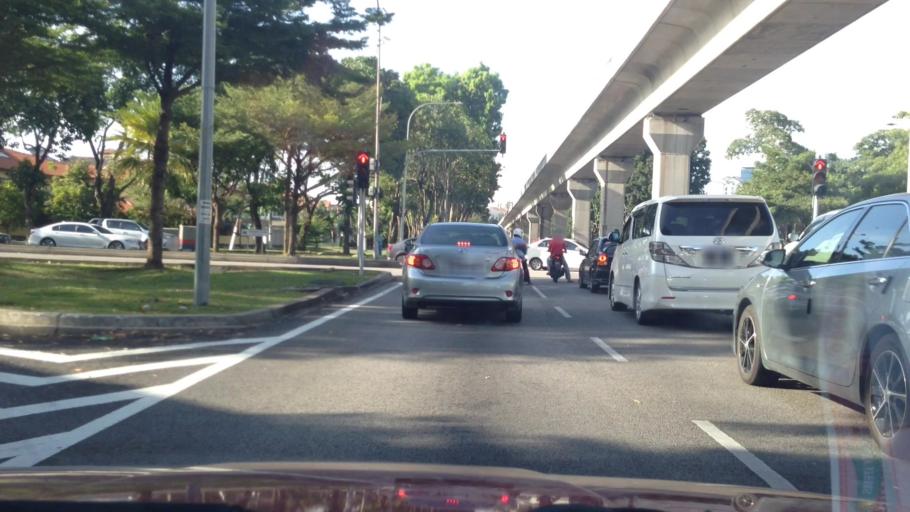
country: MY
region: Selangor
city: Subang Jaya
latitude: 3.0390
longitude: 101.5880
